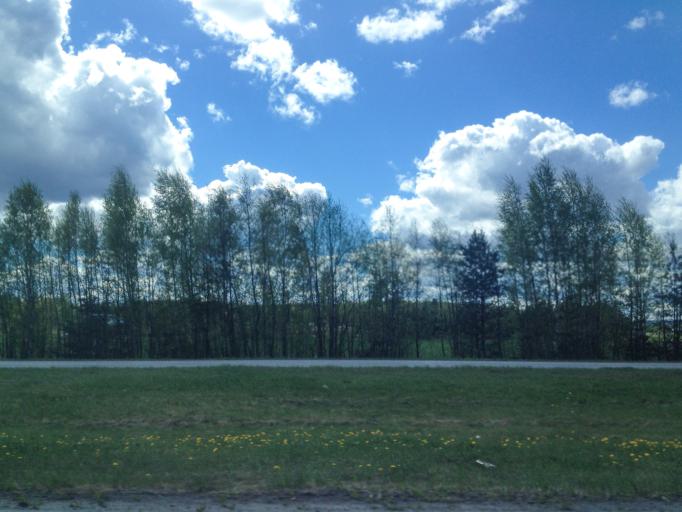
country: FI
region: Haeme
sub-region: Haemeenlinna
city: Kalvola
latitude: 61.0906
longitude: 24.1893
